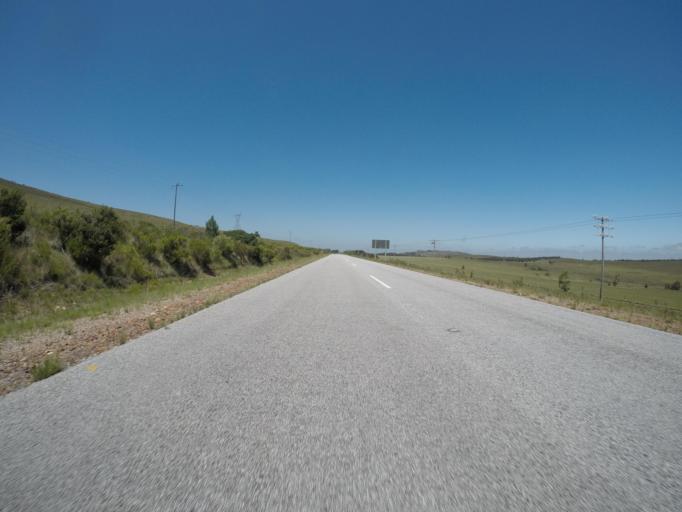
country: ZA
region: Eastern Cape
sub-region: Cacadu District Municipality
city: Kareedouw
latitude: -33.9736
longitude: 24.4795
